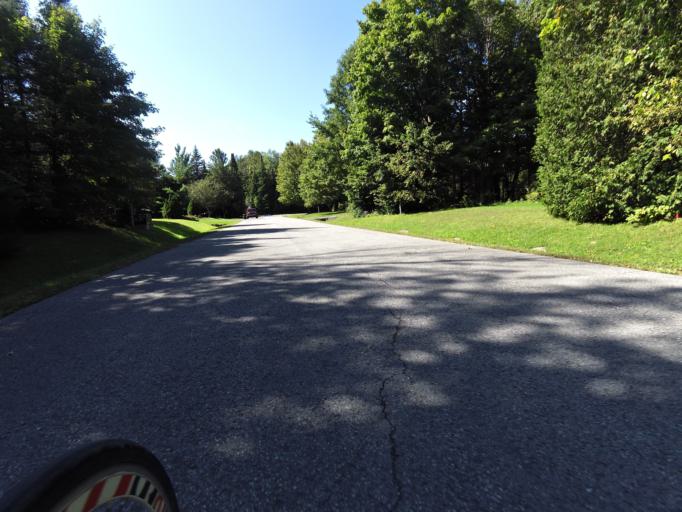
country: CA
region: Ontario
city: Bells Corners
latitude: 45.1766
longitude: -75.8267
